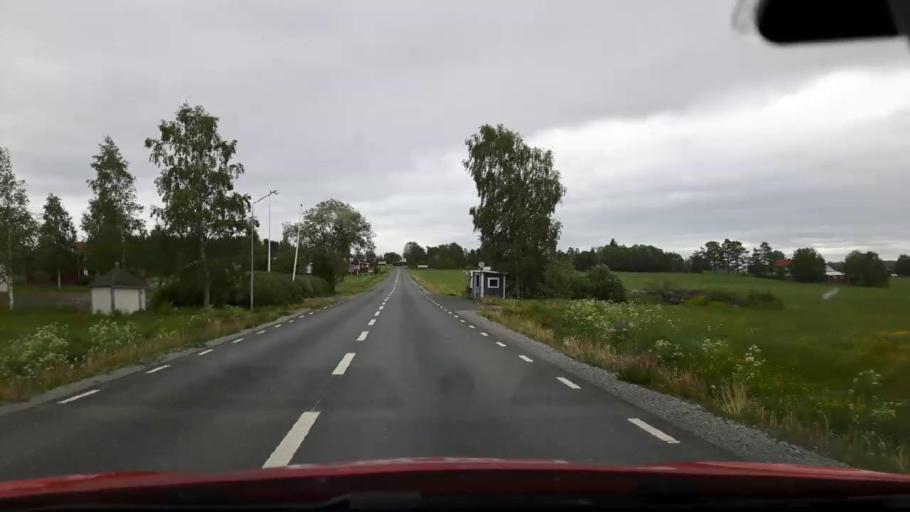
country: SE
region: Jaemtland
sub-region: OEstersunds Kommun
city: Lit
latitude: 63.7421
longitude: 14.8529
